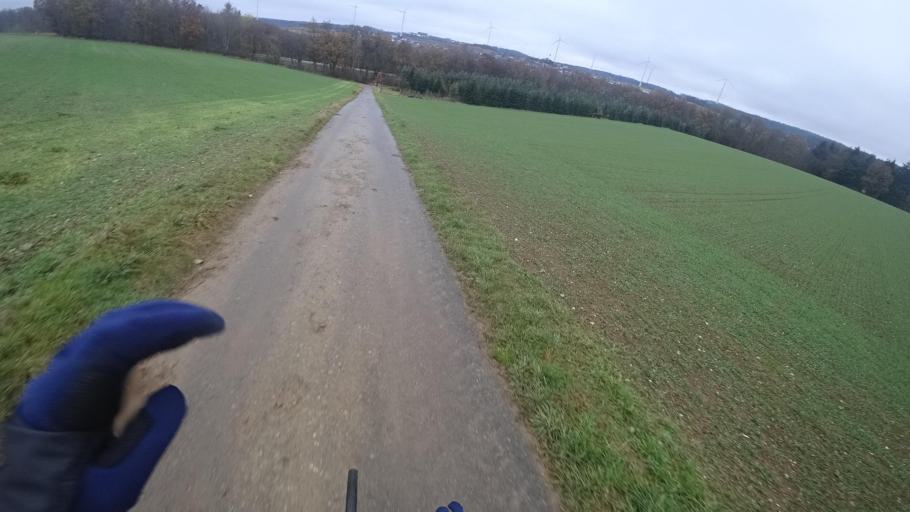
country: DE
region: Rheinland-Pfalz
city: Kratzenburg
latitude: 50.1809
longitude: 7.5489
